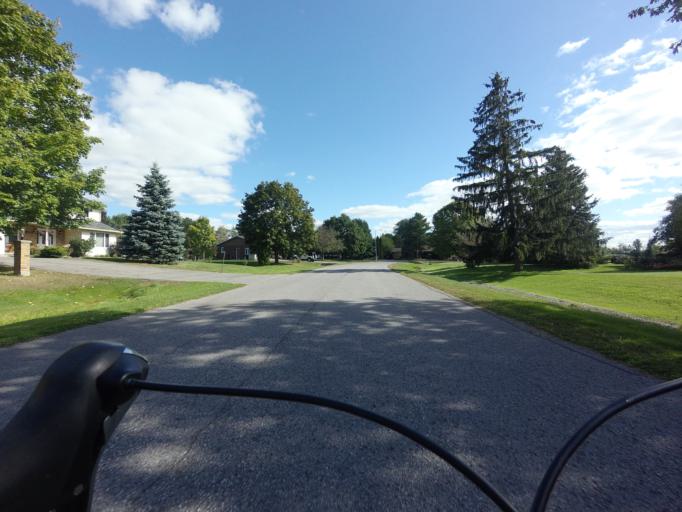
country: CA
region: Ontario
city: Bells Corners
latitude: 45.1531
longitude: -75.6538
